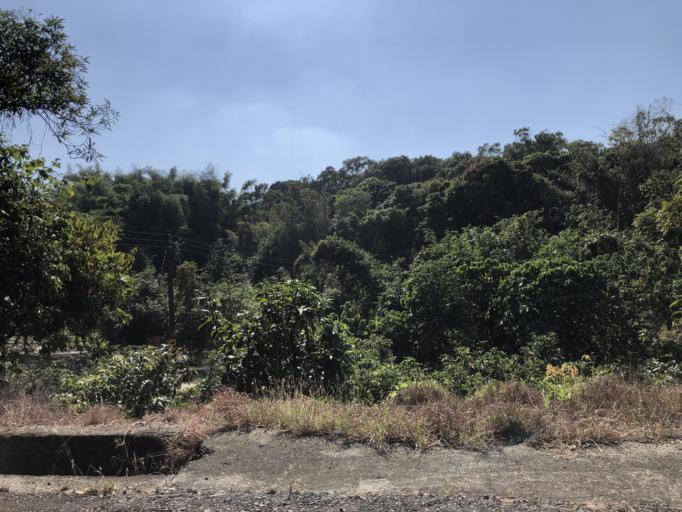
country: TW
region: Taiwan
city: Yujing
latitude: 23.0346
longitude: 120.3508
